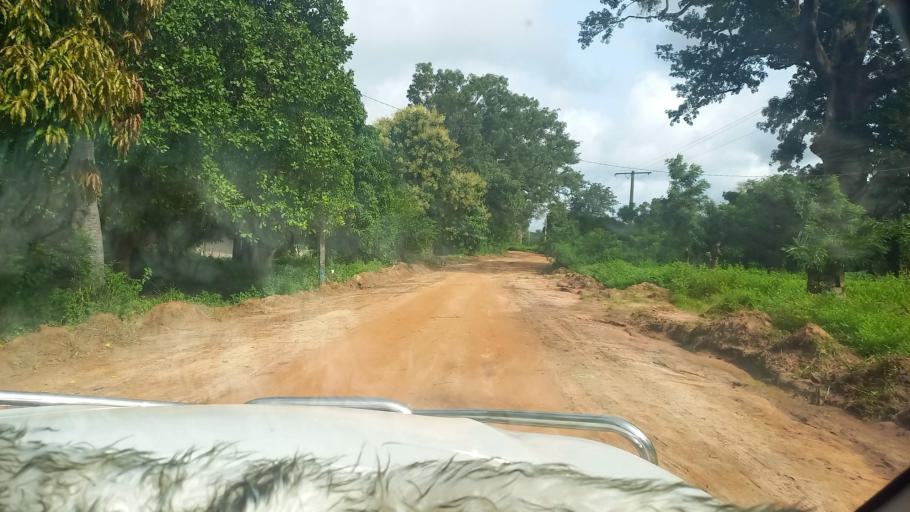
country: SN
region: Ziguinchor
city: Ziguinchor
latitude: 12.6650
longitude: -16.2655
